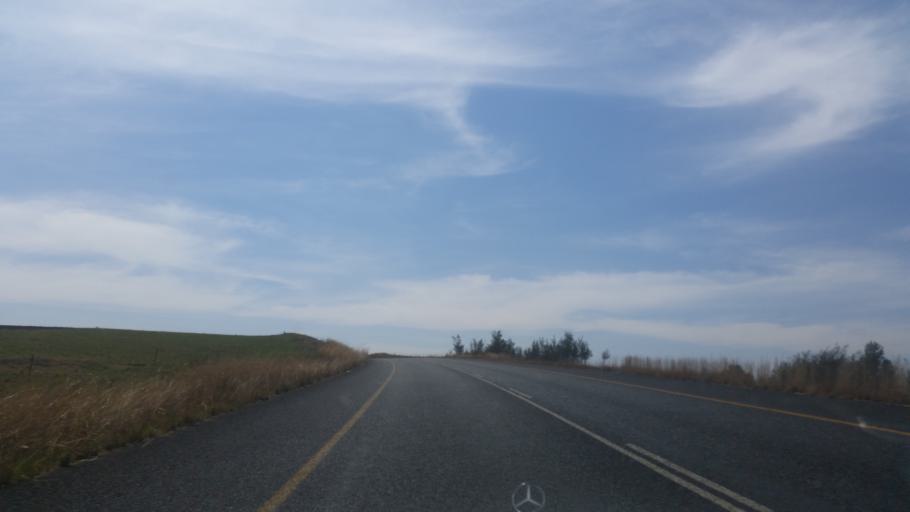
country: ZA
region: Orange Free State
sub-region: Thabo Mofutsanyana District Municipality
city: Harrismith
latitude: -28.5284
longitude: 29.0788
